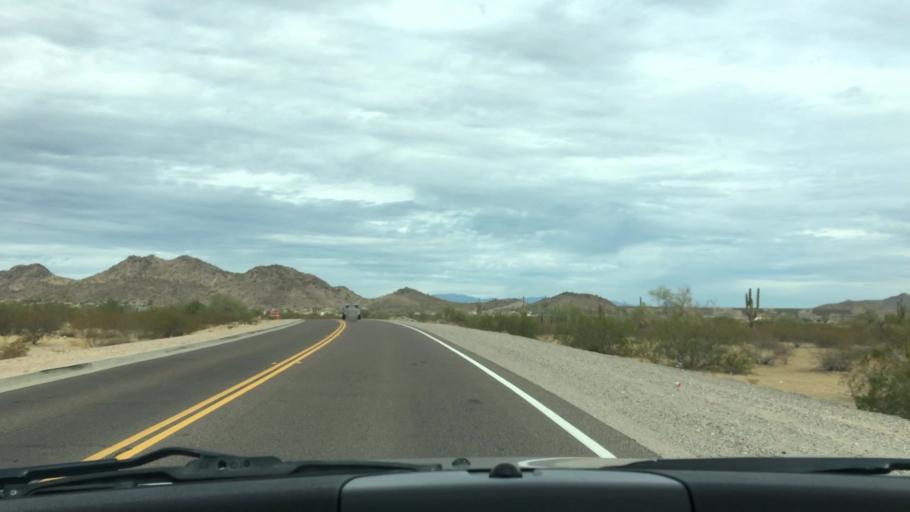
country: US
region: Arizona
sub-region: Maricopa County
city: Sun City West
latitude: 33.7184
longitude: -112.2330
